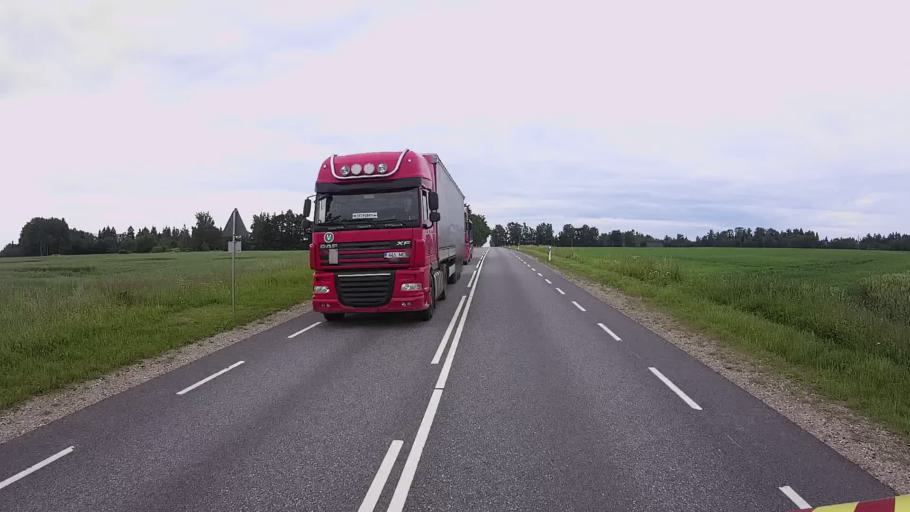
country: EE
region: Viljandimaa
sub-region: Karksi vald
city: Karksi-Nuia
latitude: 58.1375
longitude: 25.5851
